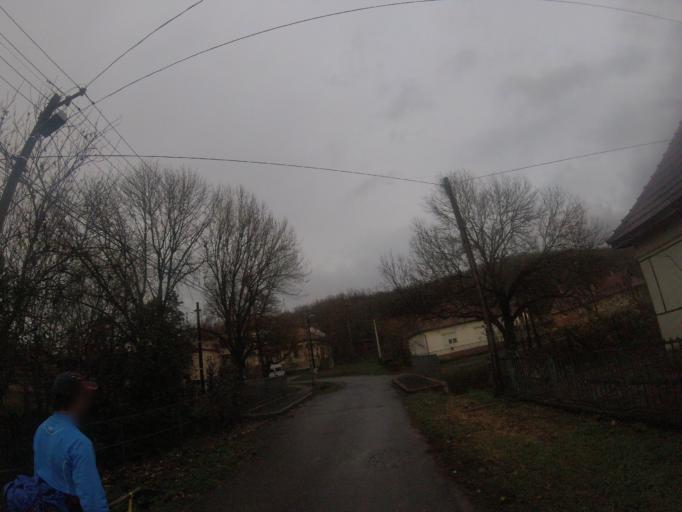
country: HU
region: Nograd
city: Rimoc
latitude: 48.0089
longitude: 19.5009
